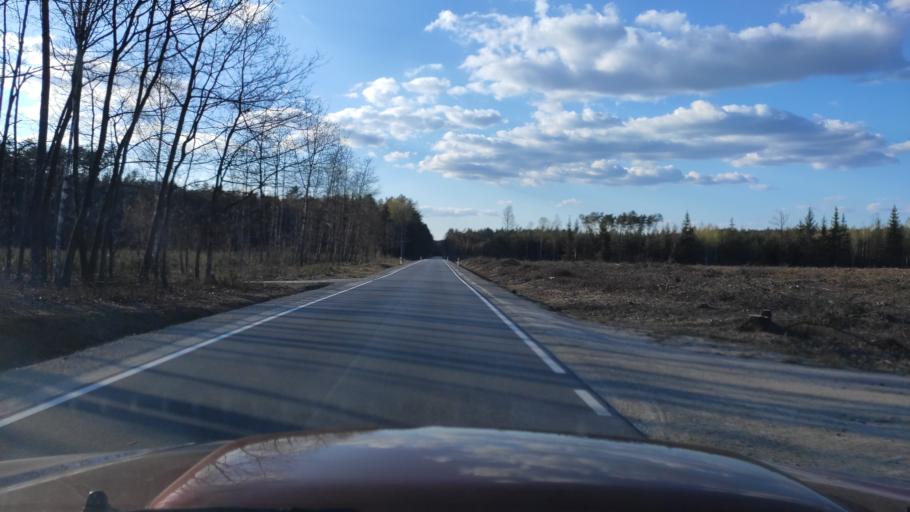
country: PL
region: Masovian Voivodeship
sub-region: Powiat zwolenski
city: Zwolen
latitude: 51.3964
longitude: 21.5425
